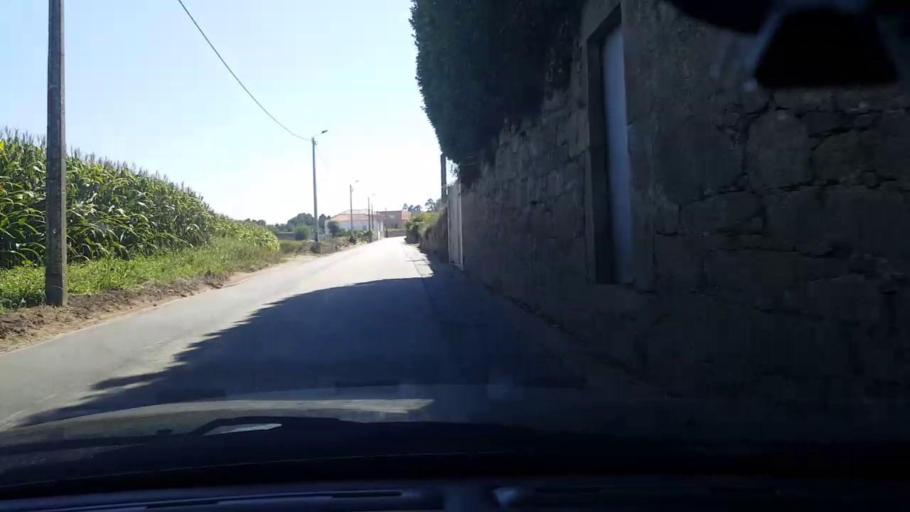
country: PT
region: Porto
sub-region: Matosinhos
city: Lavra
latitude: 41.2660
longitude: -8.6913
